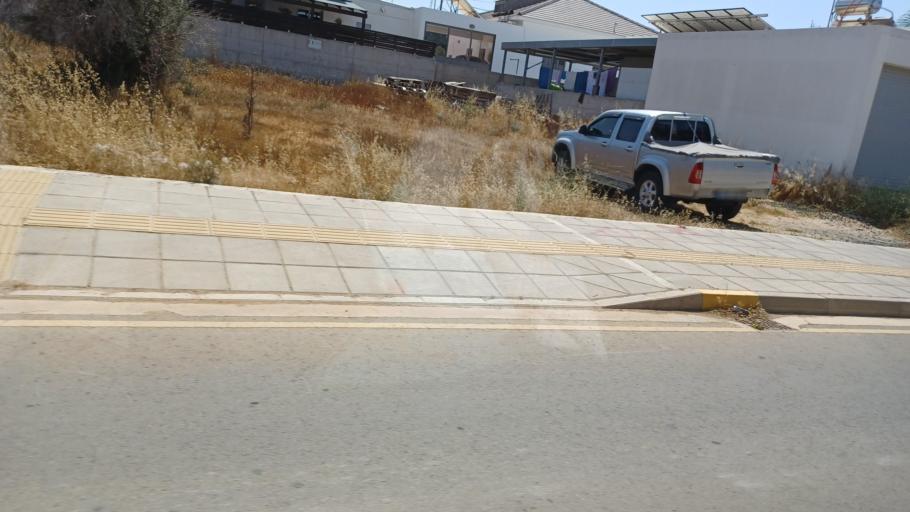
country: CY
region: Ammochostos
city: Paralimni
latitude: 35.0163
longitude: 33.9545
